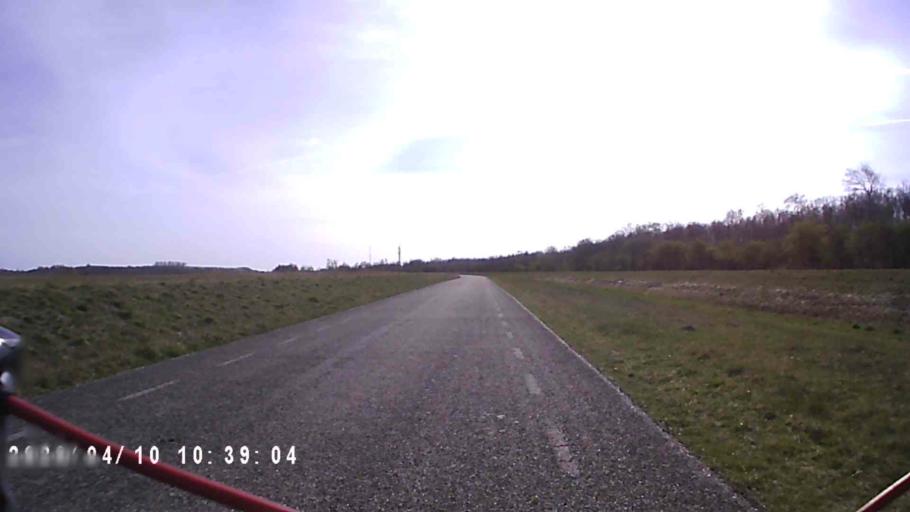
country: NL
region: Friesland
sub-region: Gemeente Dongeradeel
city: Anjum
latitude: 53.3856
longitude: 6.2251
